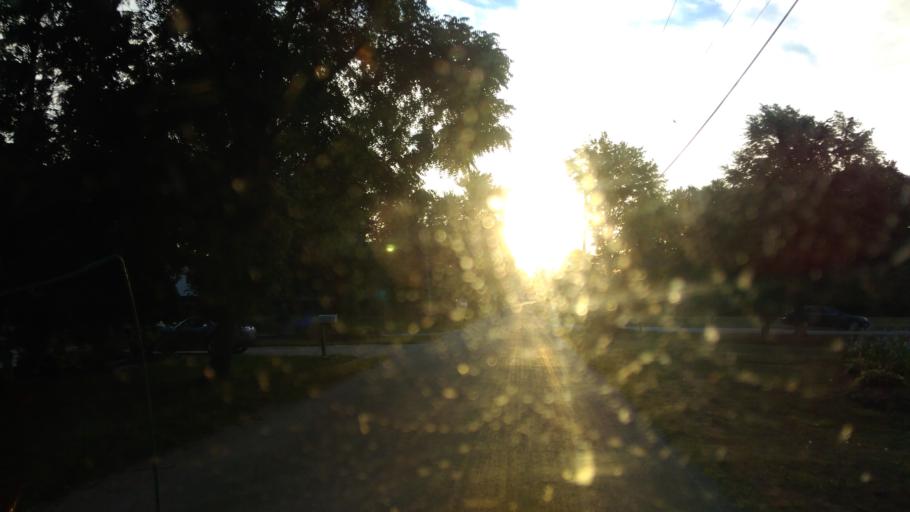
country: US
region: Indiana
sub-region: Adams County
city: Berne
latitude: 40.6419
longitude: -85.0368
